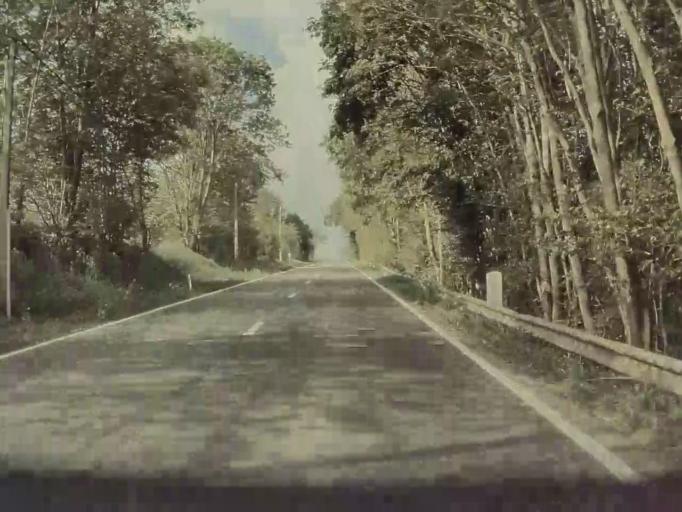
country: BE
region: Wallonia
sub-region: Province de Namur
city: Somme-Leuze
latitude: 50.3224
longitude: 5.3489
